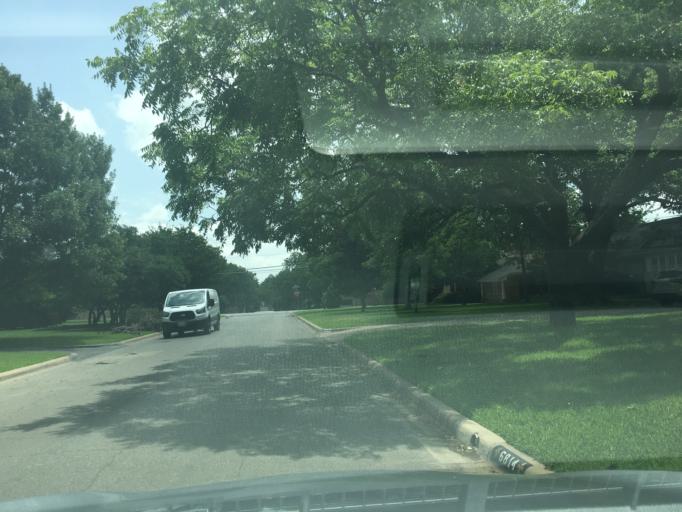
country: US
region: Texas
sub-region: Dallas County
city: University Park
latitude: 32.8746
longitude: -96.7879
